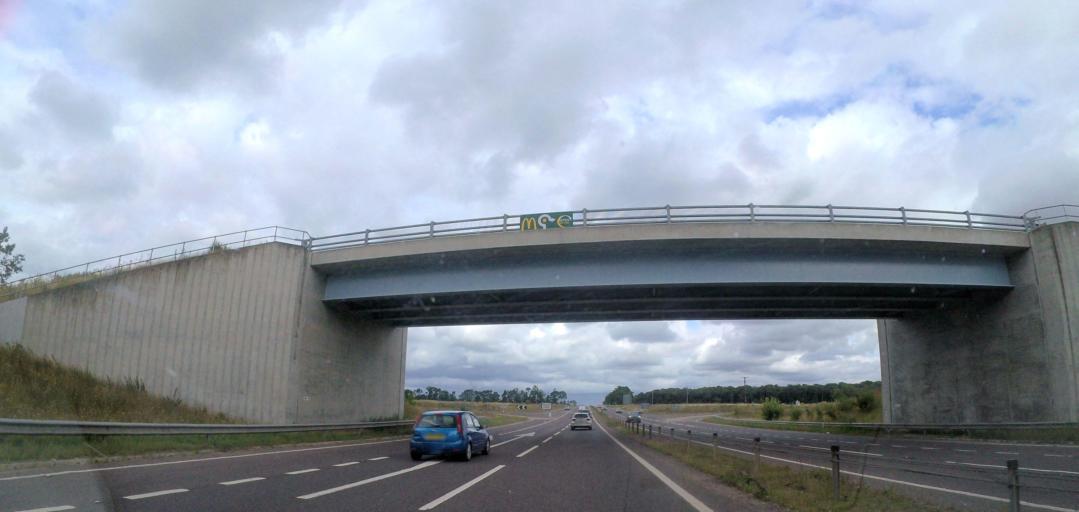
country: GB
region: England
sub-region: Norfolk
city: Weeting
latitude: 52.3887
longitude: 0.6639
